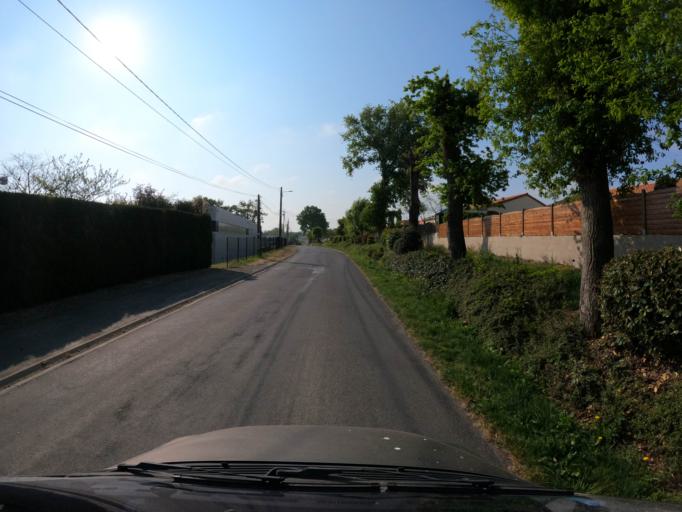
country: FR
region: Pays de la Loire
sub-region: Departement de Maine-et-Loire
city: La Romagne
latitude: 47.0584
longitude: -1.0164
